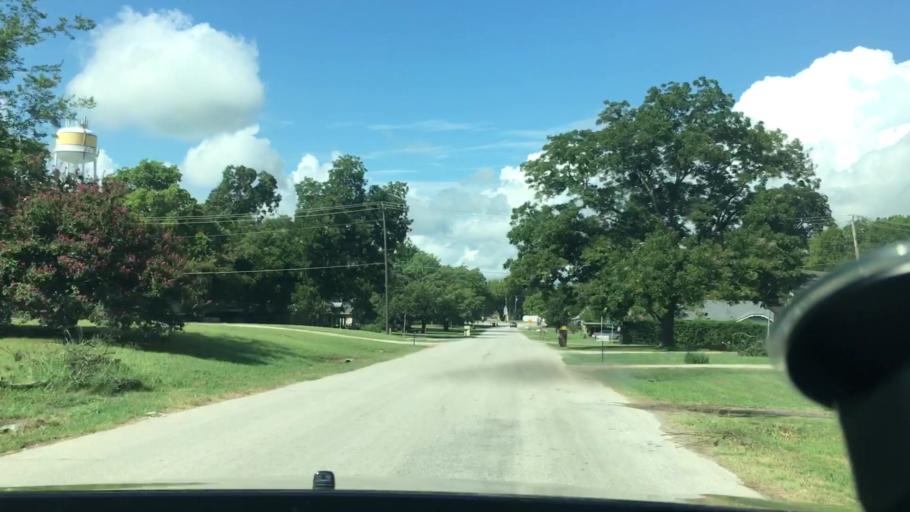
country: US
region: Oklahoma
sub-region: Marshall County
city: Madill
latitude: 34.0945
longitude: -96.7699
